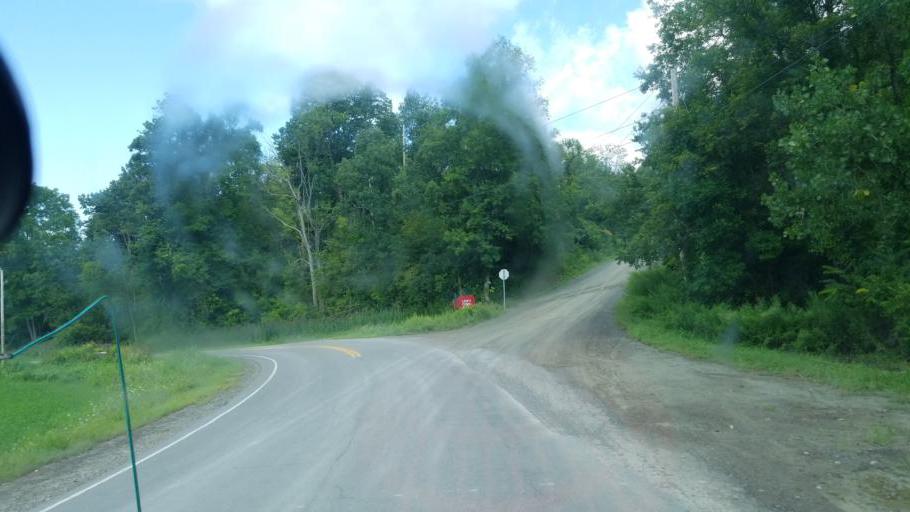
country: US
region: New York
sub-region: Steuben County
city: Canisteo
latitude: 42.2931
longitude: -77.6172
